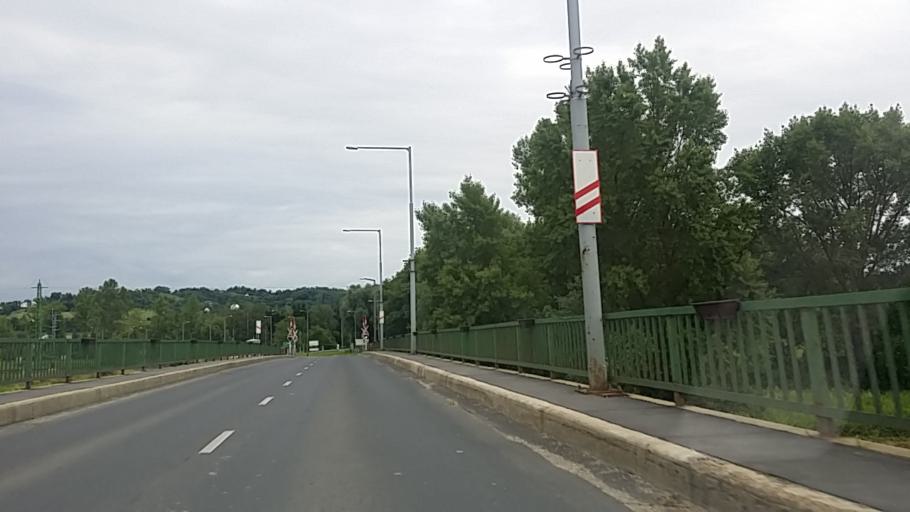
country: HU
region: Zala
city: Zalaegerszeg
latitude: 46.8592
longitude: 16.8011
